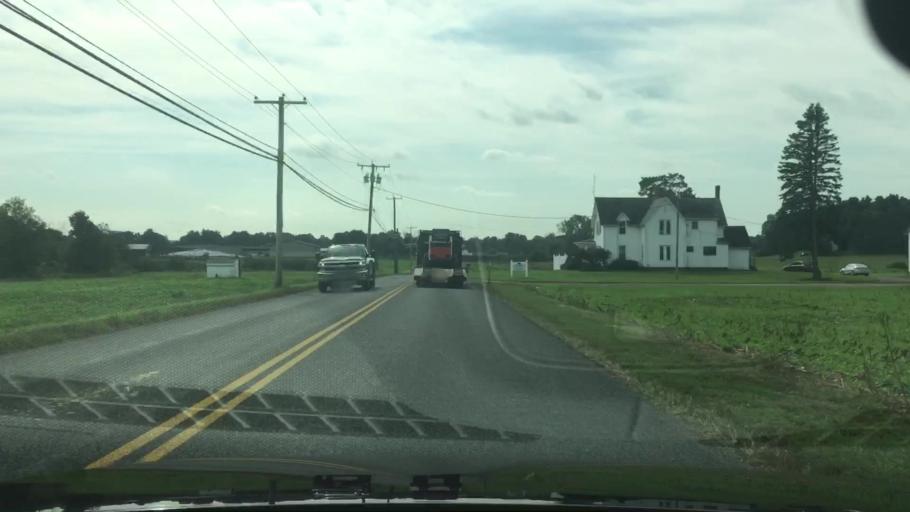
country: US
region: Connecticut
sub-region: Tolland County
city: Ellington
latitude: 41.9158
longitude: -72.4755
